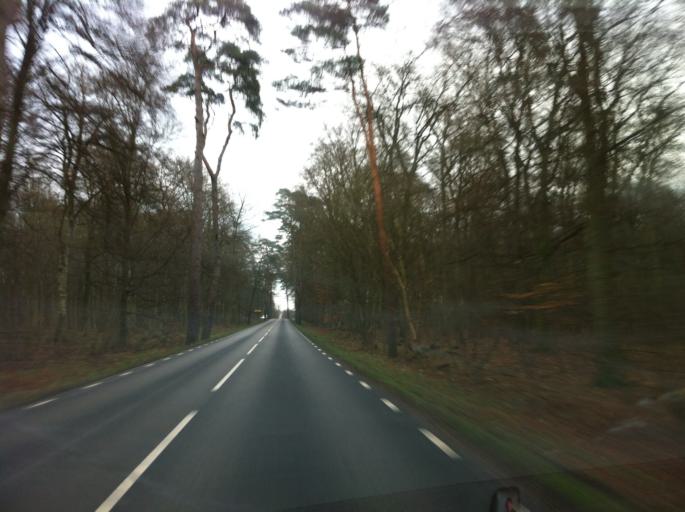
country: SE
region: Skane
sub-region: Sjobo Kommun
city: Sjoebo
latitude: 55.6920
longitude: 13.6217
